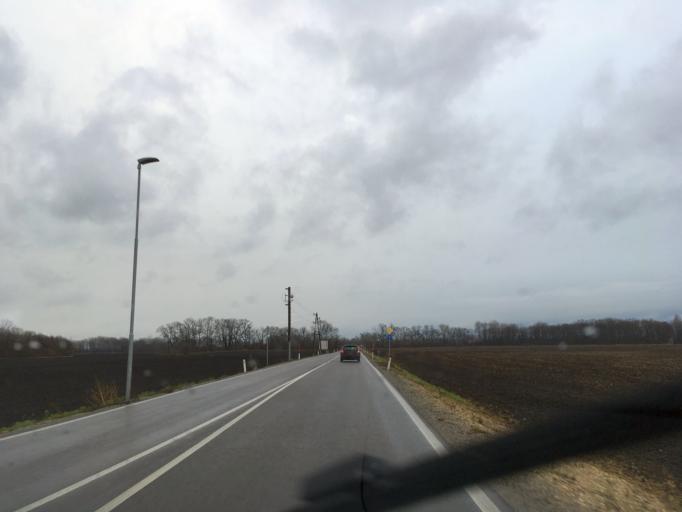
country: AT
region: Lower Austria
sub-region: Politischer Bezirk Wien-Umgebung
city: Ebergassing
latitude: 48.0428
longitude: 16.5249
